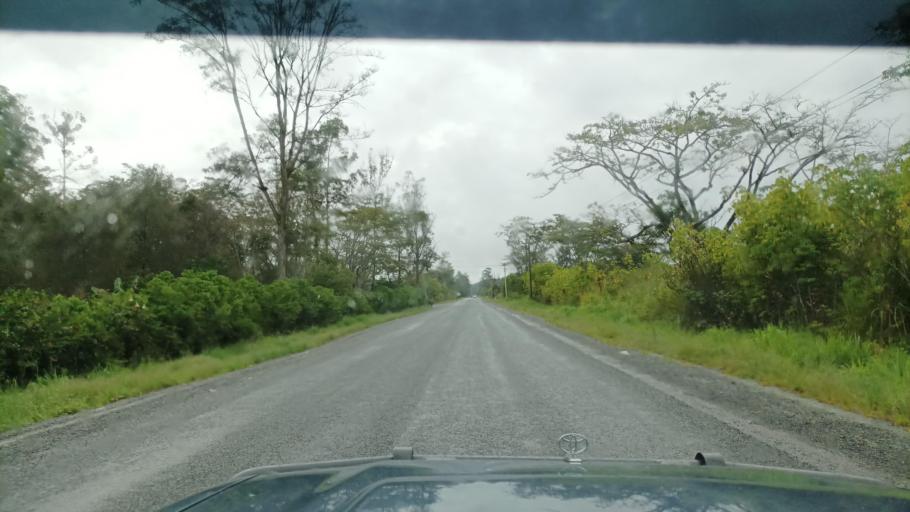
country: PG
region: Western Highlands
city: Rauna
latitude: -5.8237
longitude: 144.3924
